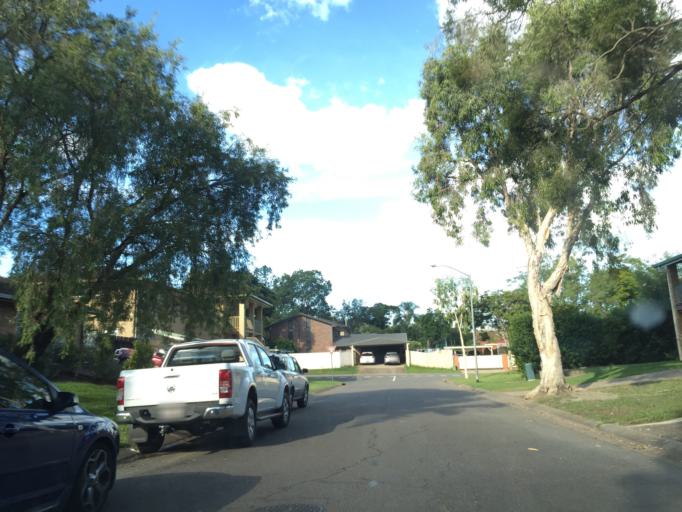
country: AU
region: Queensland
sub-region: Moreton Bay
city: Ferny Hills
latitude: -27.4367
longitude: 152.9310
